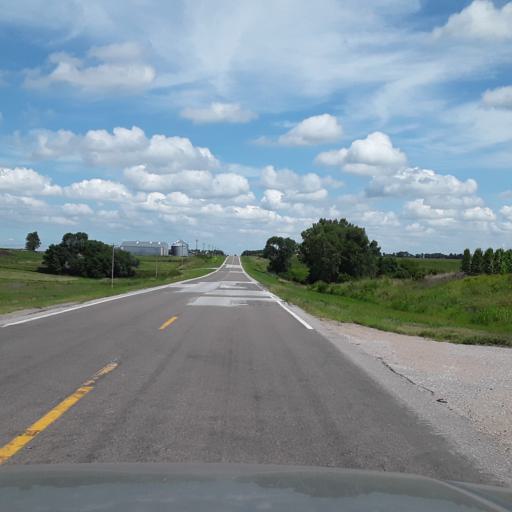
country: US
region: Nebraska
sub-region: Polk County
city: Osceola
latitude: 41.0902
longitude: -97.4258
